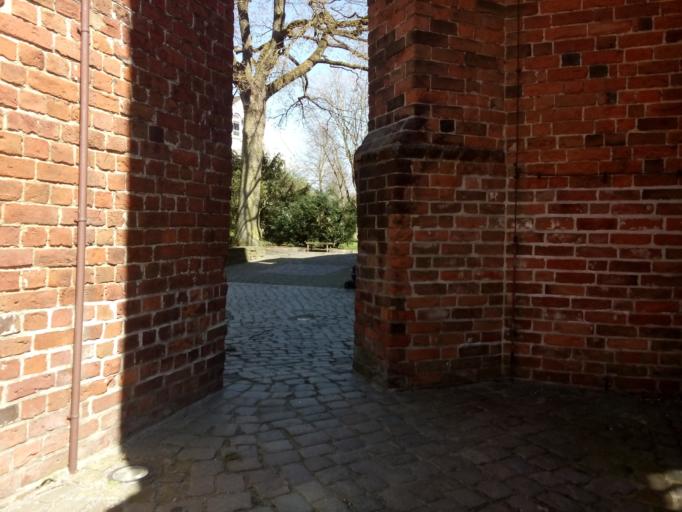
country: DE
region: Lower Saxony
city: Osterholz-Scharmbeck
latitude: 53.2245
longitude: 8.8120
